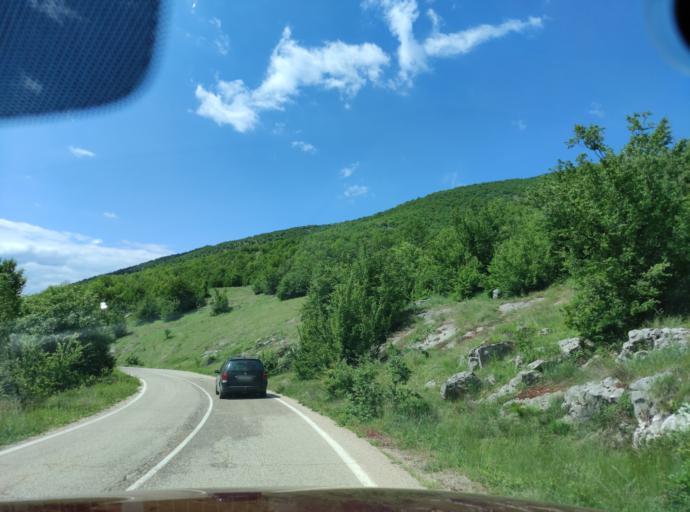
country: BG
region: Montana
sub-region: Obshtina Chiprovtsi
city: Chiprovtsi
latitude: 43.4921
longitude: 22.8039
